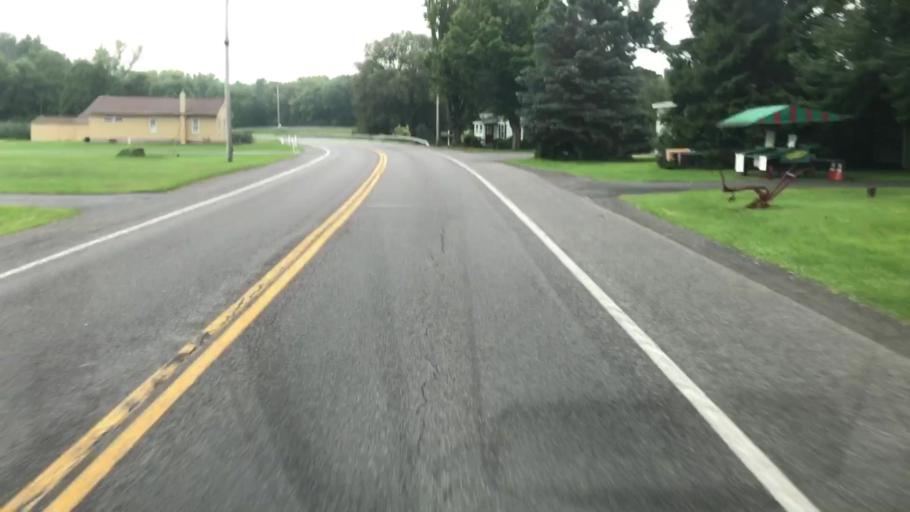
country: US
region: New York
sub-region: Onondaga County
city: Liverpool
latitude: 43.1586
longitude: -76.1944
